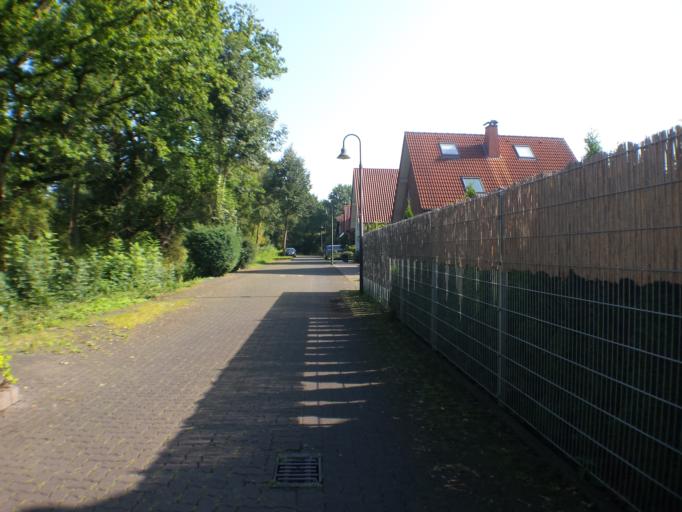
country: DE
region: North Rhine-Westphalia
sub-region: Regierungsbezirk Arnsberg
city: Lippstadt
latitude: 51.6845
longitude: 8.3244
